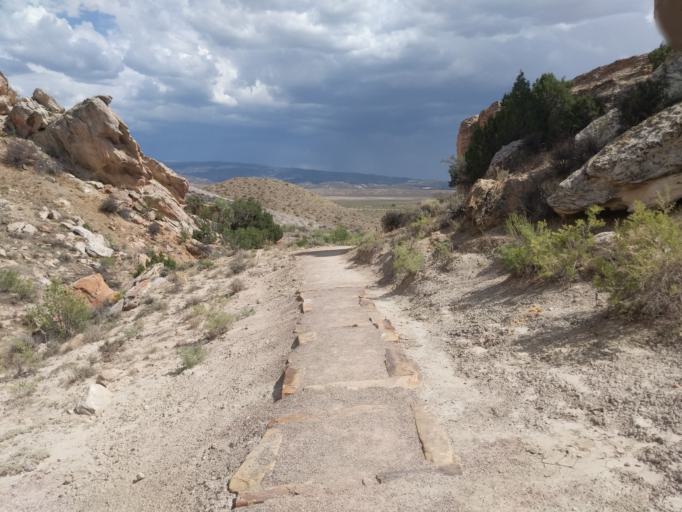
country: US
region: Utah
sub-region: Uintah County
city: Naples
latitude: 40.4391
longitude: -109.2988
